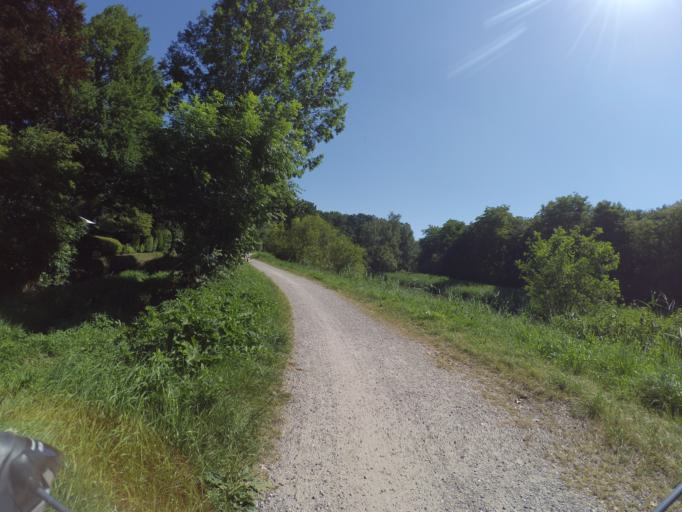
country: NL
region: North Brabant
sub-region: Gemeente Dongen
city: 's Gravenmoer
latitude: 51.6582
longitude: 4.9343
